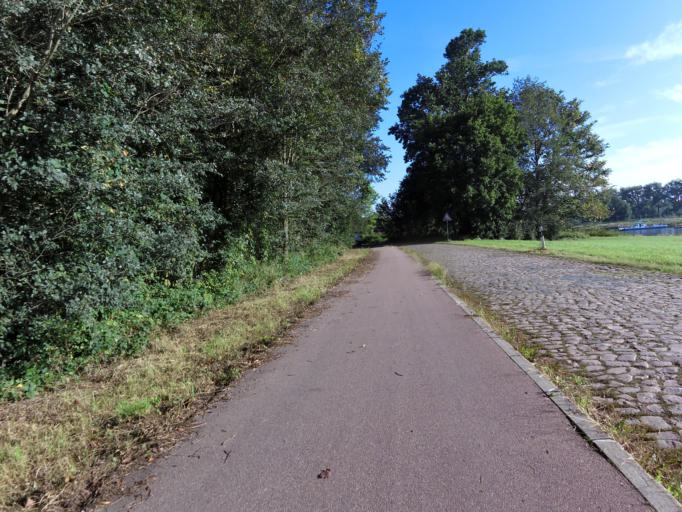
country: DE
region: Saxony-Anhalt
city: Coswig
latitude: 51.8756
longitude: 12.4502
